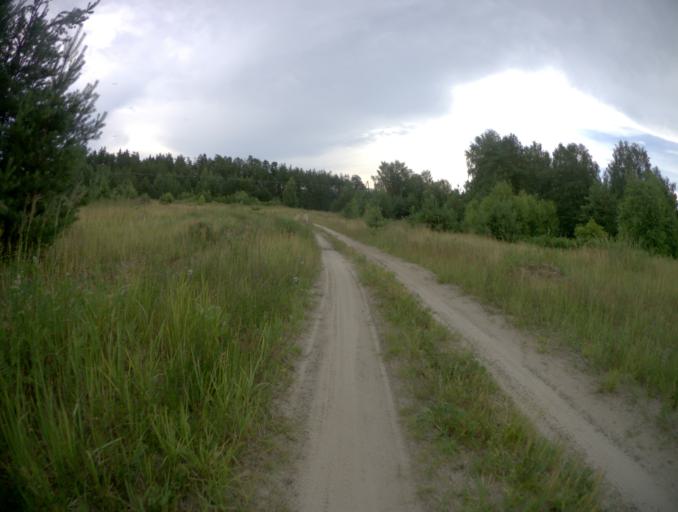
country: RU
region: Nizjnij Novgorod
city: Frolishchi
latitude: 56.5633
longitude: 42.5293
